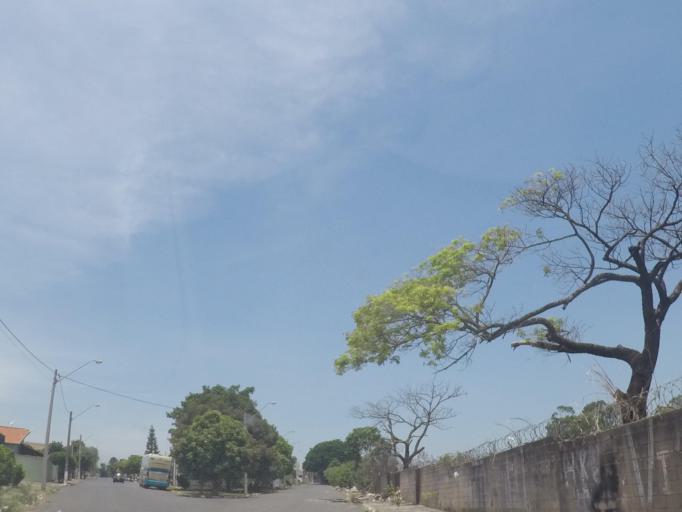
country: BR
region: Sao Paulo
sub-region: Hortolandia
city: Hortolandia
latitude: -22.8591
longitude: -47.1855
